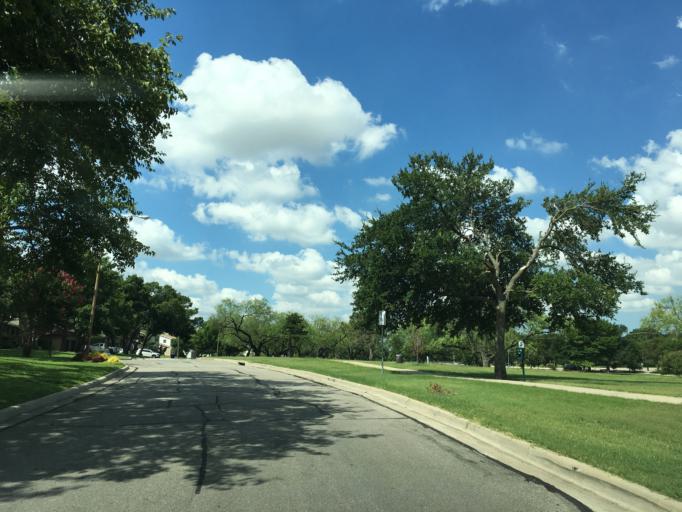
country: US
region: Texas
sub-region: Dallas County
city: Farmers Branch
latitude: 32.9291
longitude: -96.8797
